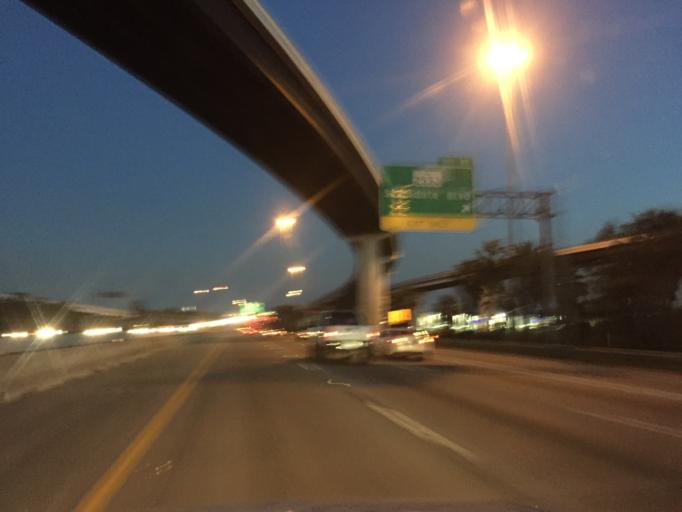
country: US
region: Texas
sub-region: Harris County
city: South Houston
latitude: 29.6059
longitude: -95.2050
